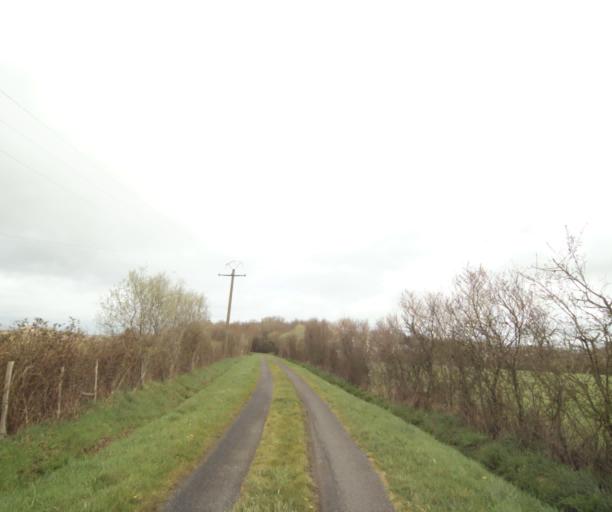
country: FR
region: Pays de la Loire
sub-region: Departement de la Loire-Atlantique
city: Bouvron
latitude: 47.4268
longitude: -1.8922
